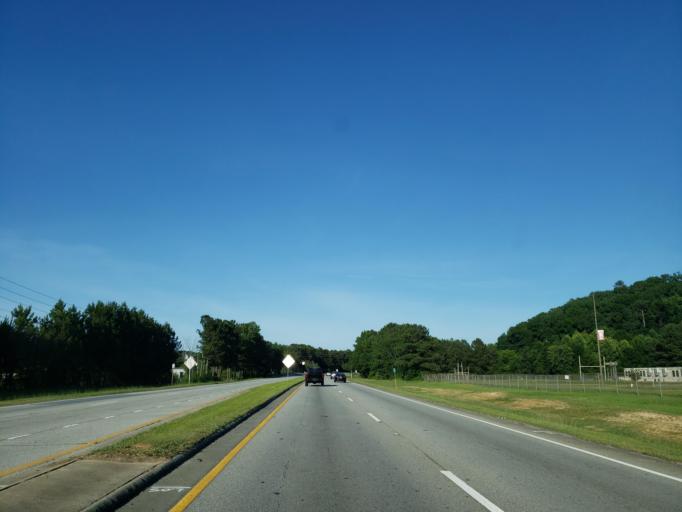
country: US
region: Georgia
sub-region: Floyd County
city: Rome
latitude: 34.2885
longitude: -85.1495
